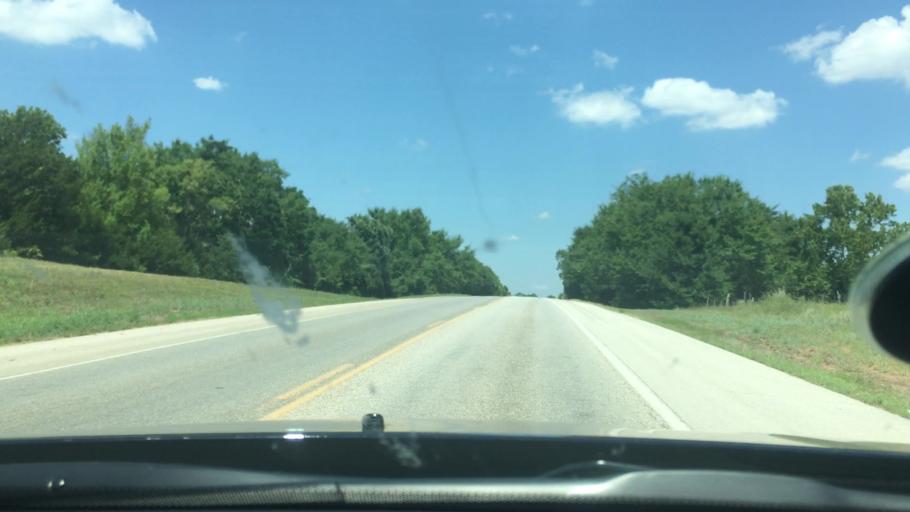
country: US
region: Oklahoma
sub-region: Marshall County
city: Oakland
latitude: 34.1782
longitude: -96.8620
